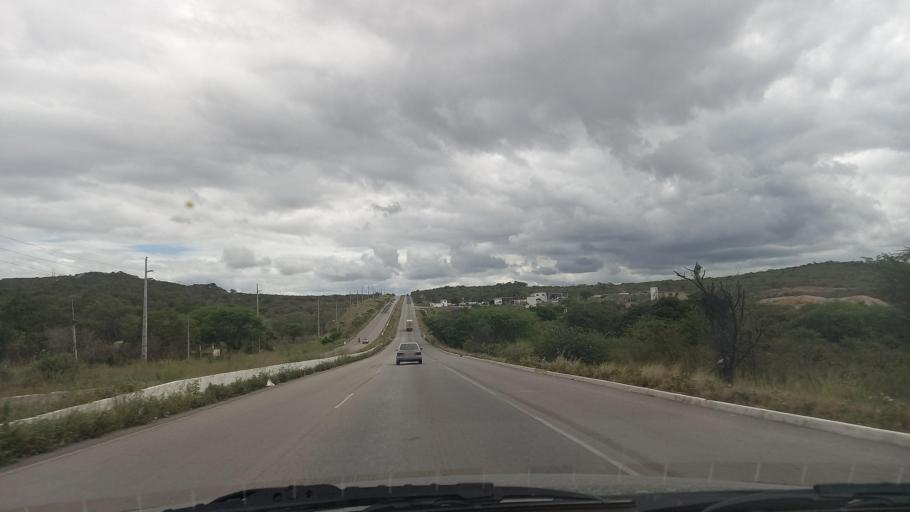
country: BR
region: Pernambuco
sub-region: Caruaru
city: Caruaru
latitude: -8.3131
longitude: -36.0406
